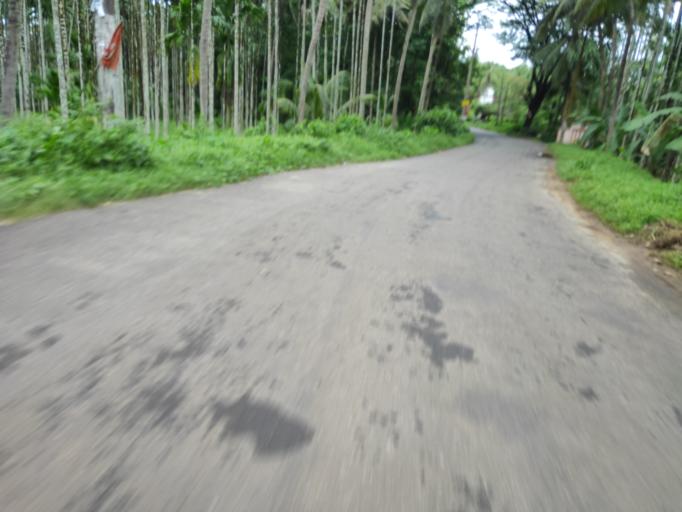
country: IN
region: Kerala
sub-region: Malappuram
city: Manjeri
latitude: 11.1853
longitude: 76.2058
